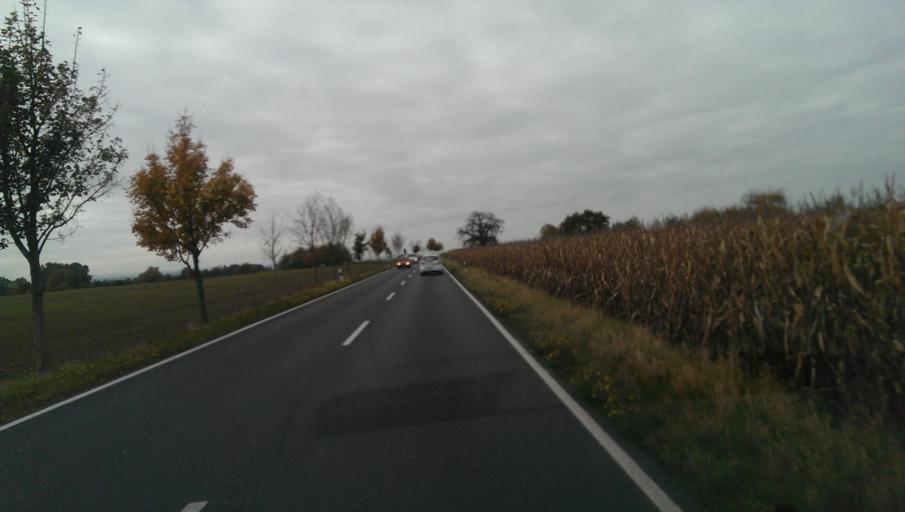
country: DE
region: Saxony
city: Lohmen
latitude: 50.9836
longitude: 13.9815
